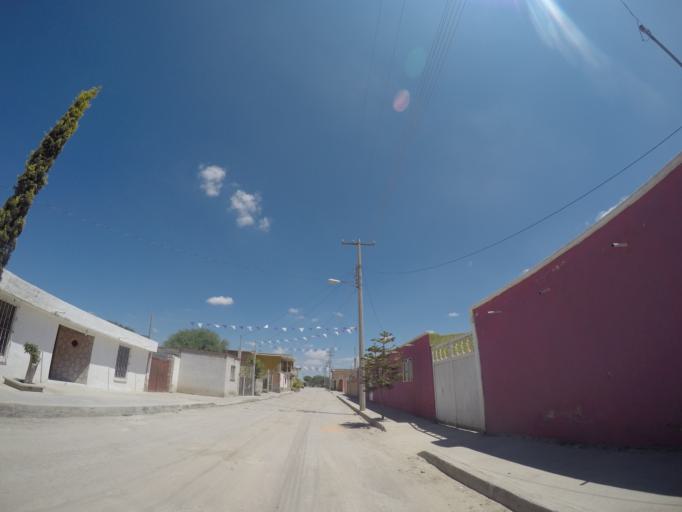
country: MX
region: San Luis Potosi
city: La Pila
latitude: 22.0006
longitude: -100.8979
